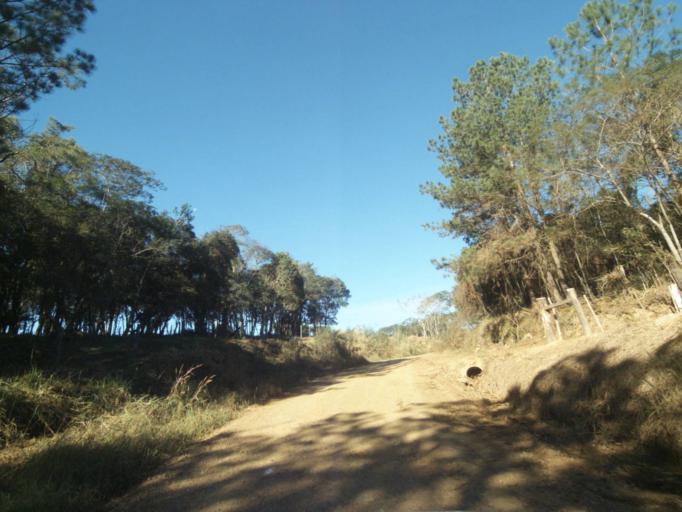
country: BR
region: Parana
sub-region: Tibagi
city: Tibagi
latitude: -24.5403
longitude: -50.5015
